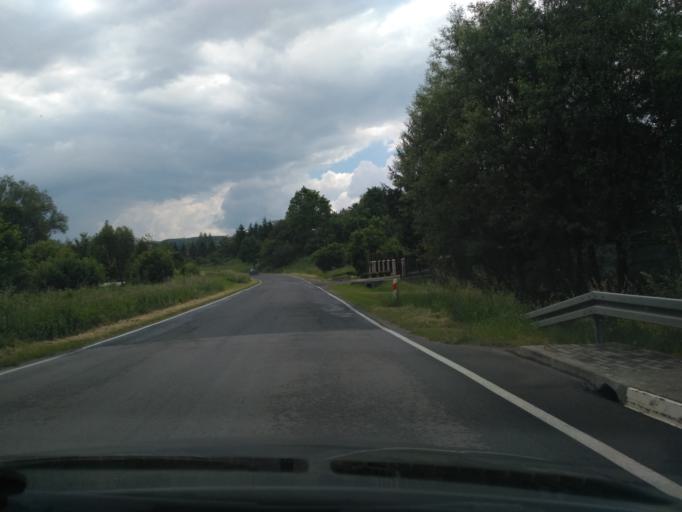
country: PL
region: Subcarpathian Voivodeship
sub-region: Powiat przeworski
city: Jawornik Polski
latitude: 49.9098
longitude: 22.3048
